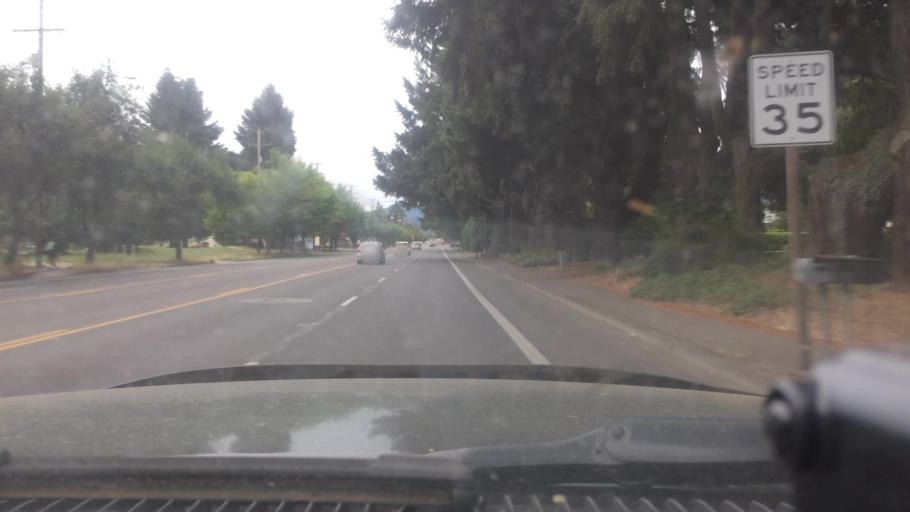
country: US
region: Oregon
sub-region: Lane County
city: Eugene
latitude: 44.0739
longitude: -123.1191
